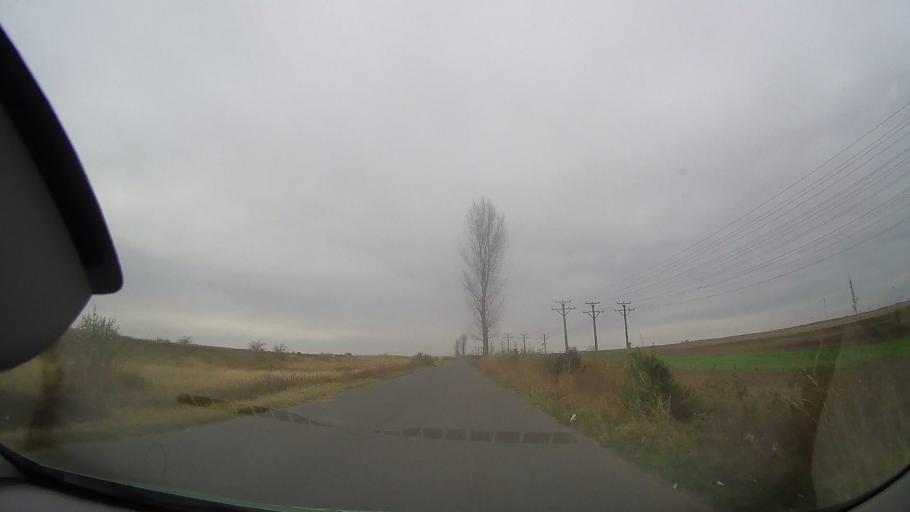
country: RO
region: Braila
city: Dudesti
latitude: 44.9018
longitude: 27.4322
